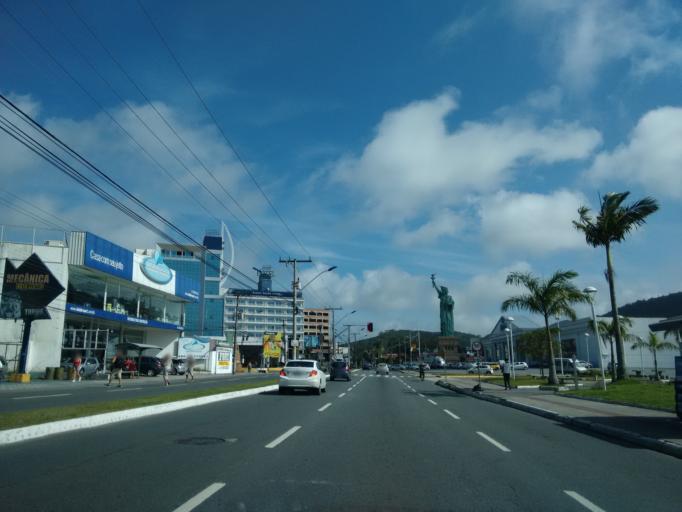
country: BR
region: Santa Catarina
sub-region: Itajai
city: Itajai
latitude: -26.9190
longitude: -48.6543
